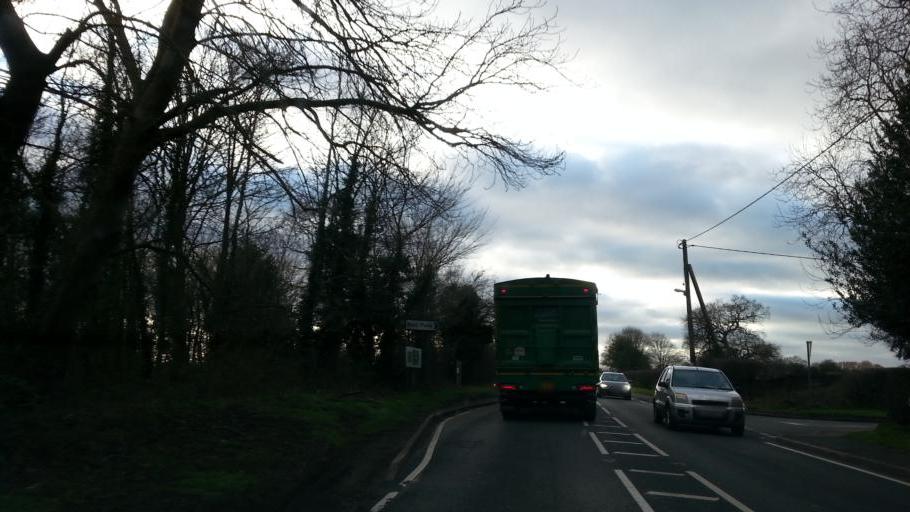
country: GB
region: England
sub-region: Suffolk
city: Great Barton
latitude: 52.2638
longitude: 0.7638
